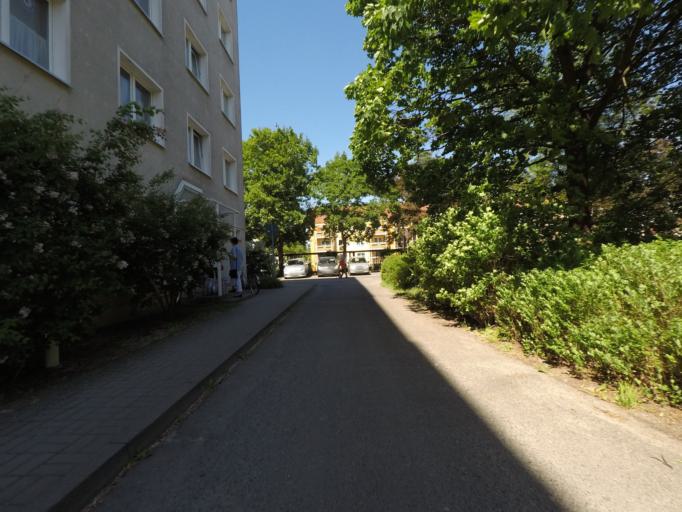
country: DE
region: Brandenburg
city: Melchow
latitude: 52.8360
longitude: 13.7423
